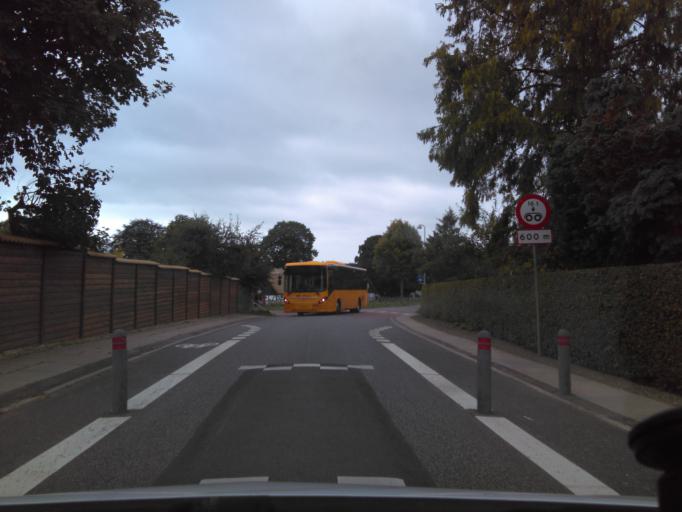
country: DK
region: Capital Region
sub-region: Fureso Kommune
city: Farum
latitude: 55.8089
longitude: 12.3432
